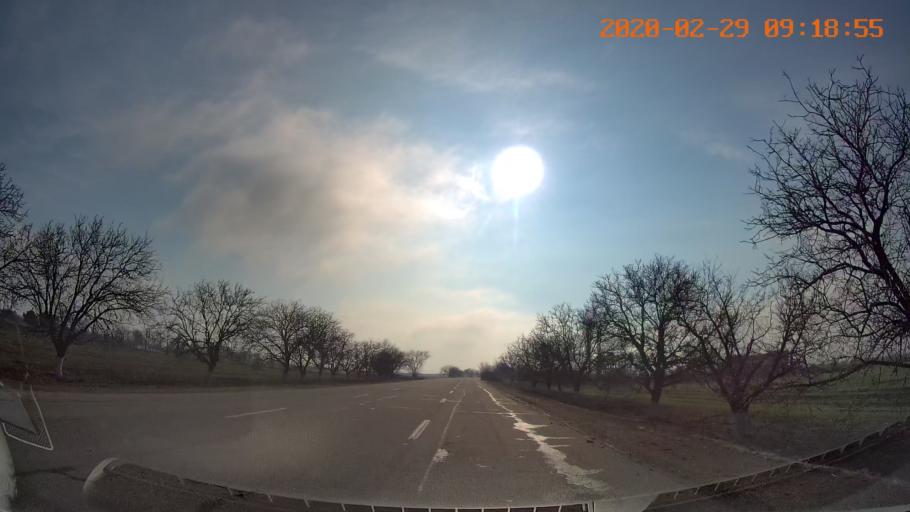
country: MD
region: Telenesti
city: Pervomaisc
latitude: 46.7690
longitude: 29.9320
